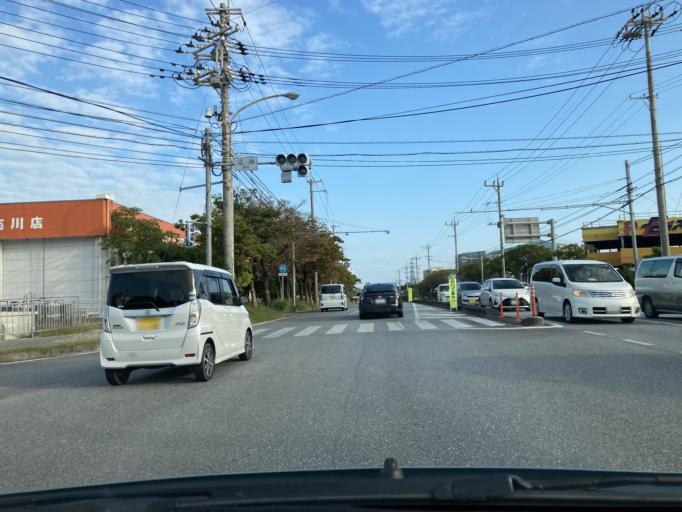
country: JP
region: Okinawa
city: Okinawa
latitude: 26.3476
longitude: 127.8340
